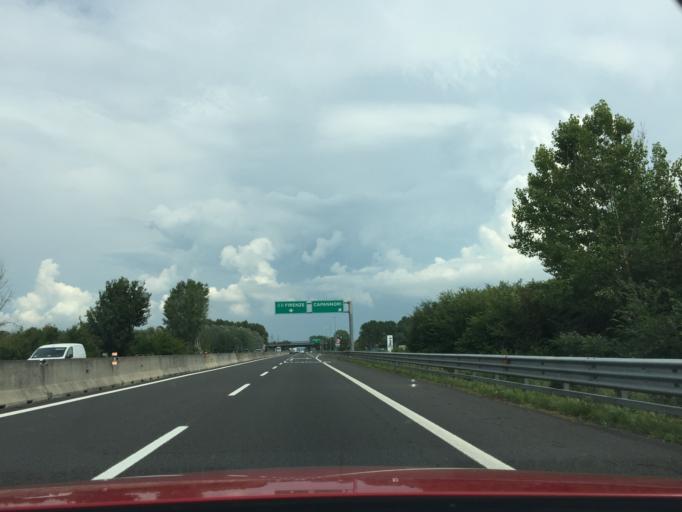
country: IT
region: Tuscany
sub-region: Provincia di Lucca
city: Capannori
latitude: 43.8235
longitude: 10.5881
